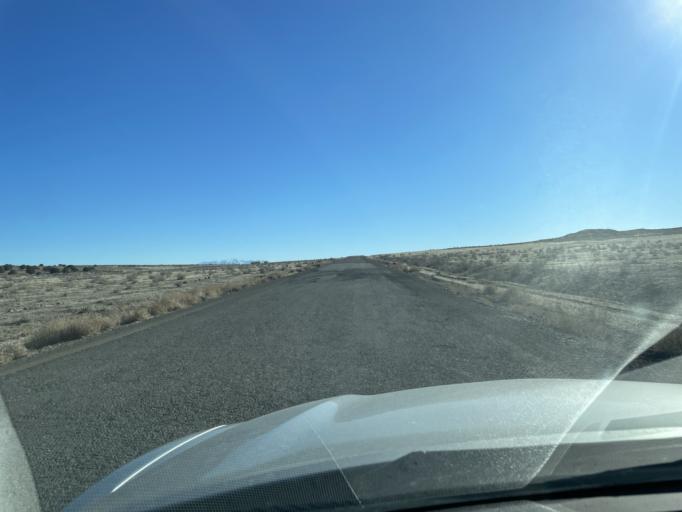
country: US
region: Colorado
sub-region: Mesa County
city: Loma
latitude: 39.1837
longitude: -109.1287
